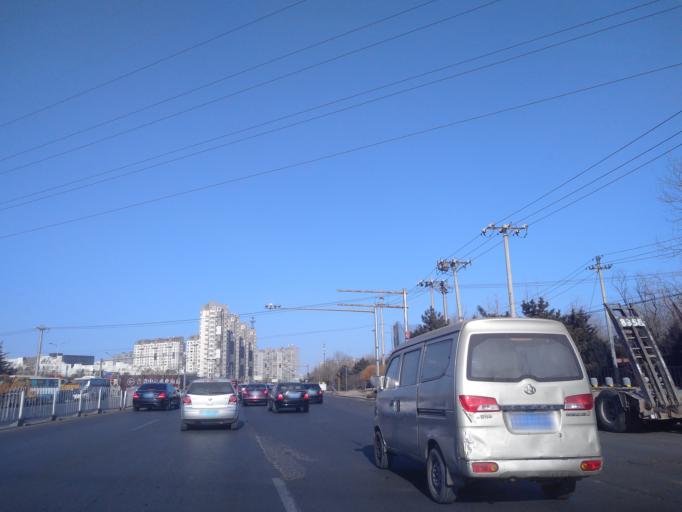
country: CN
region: Beijing
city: Jiugong
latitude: 39.8233
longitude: 116.4759
